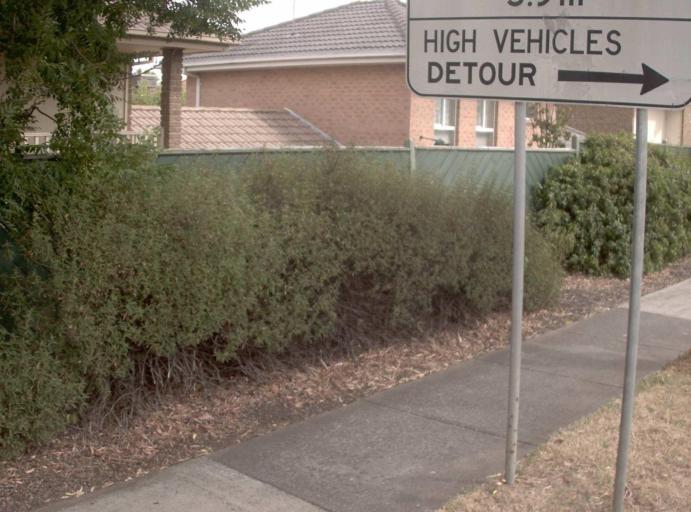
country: AU
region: Victoria
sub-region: Monash
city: Chadstone
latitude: -37.8831
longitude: 145.1089
